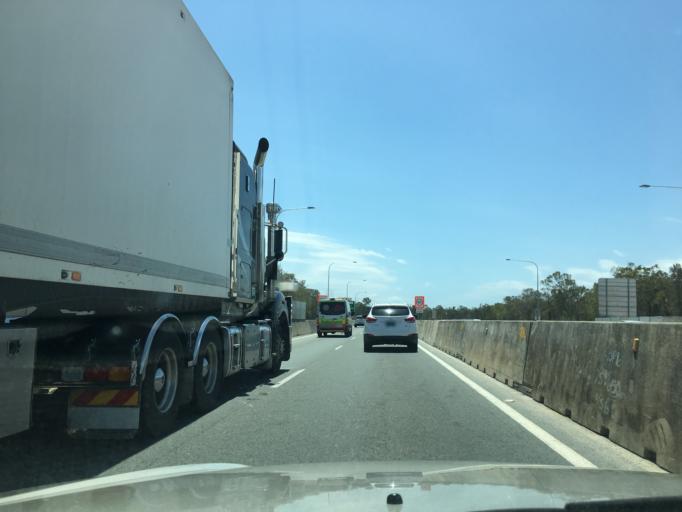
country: AU
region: Queensland
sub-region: Brisbane
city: Deagon
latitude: -27.3474
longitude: 153.0773
